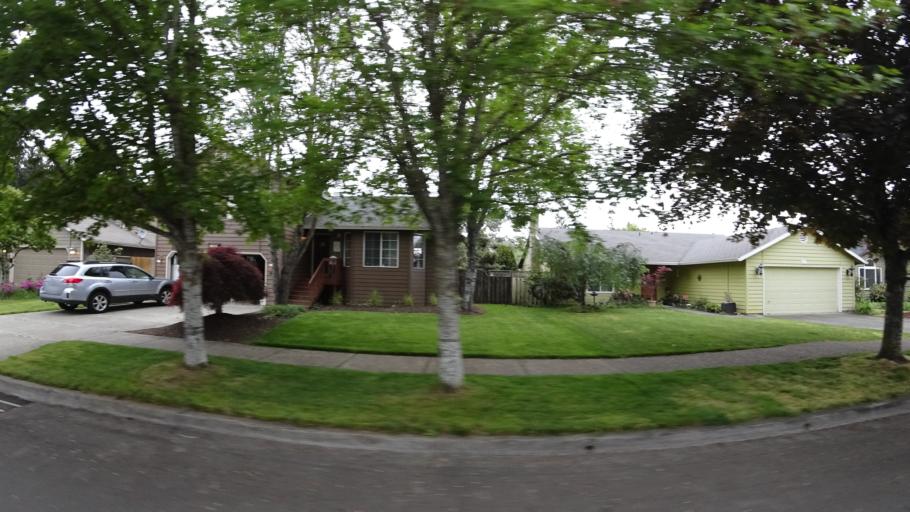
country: US
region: Oregon
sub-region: Washington County
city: Aloha
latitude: 45.5057
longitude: -122.9108
